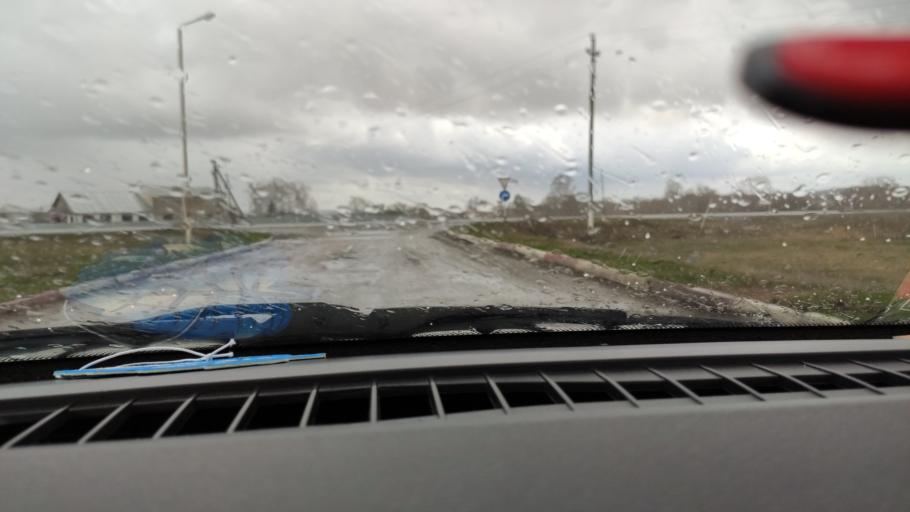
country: RU
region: Samara
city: Koshki
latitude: 54.1620
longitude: 50.4107
